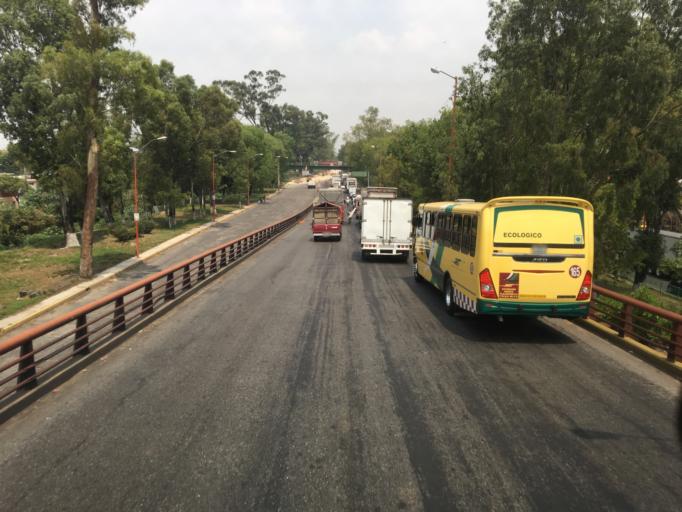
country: MX
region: Mexico
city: Tlalnepantla
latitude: 19.5275
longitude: -99.1600
